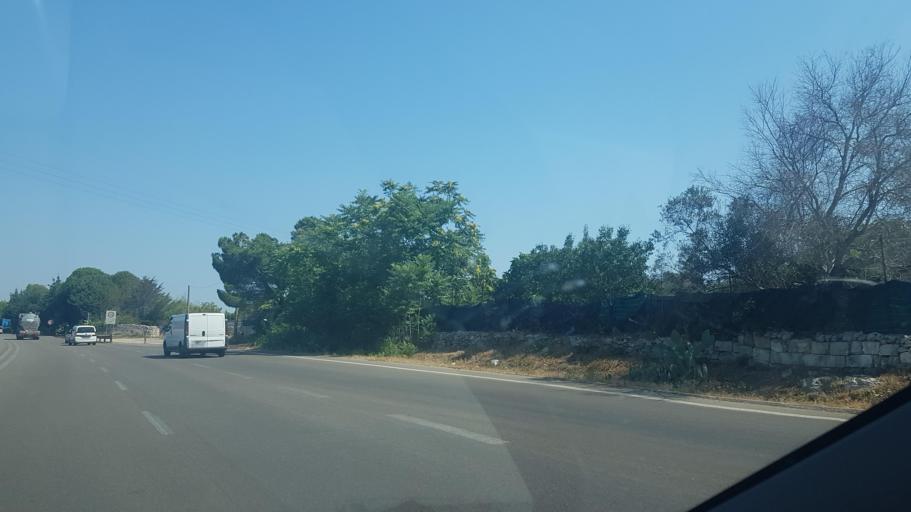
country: IT
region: Apulia
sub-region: Provincia di Lecce
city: Muro Leccese
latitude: 40.1175
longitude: 18.3205
